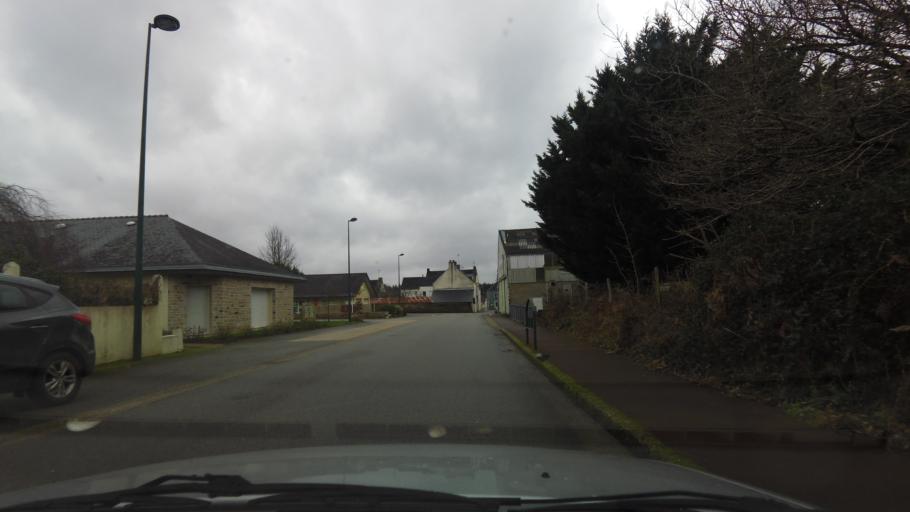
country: FR
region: Brittany
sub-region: Departement du Morbihan
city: Elven
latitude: 47.7933
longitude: -2.5910
